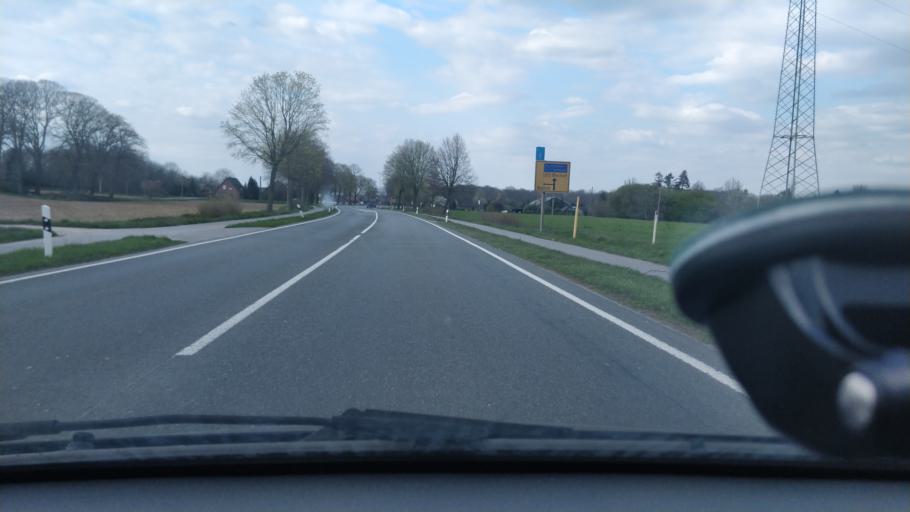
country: DE
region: North Rhine-Westphalia
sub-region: Regierungsbezirk Dusseldorf
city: Hamminkeln
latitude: 51.7181
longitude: 6.5962
